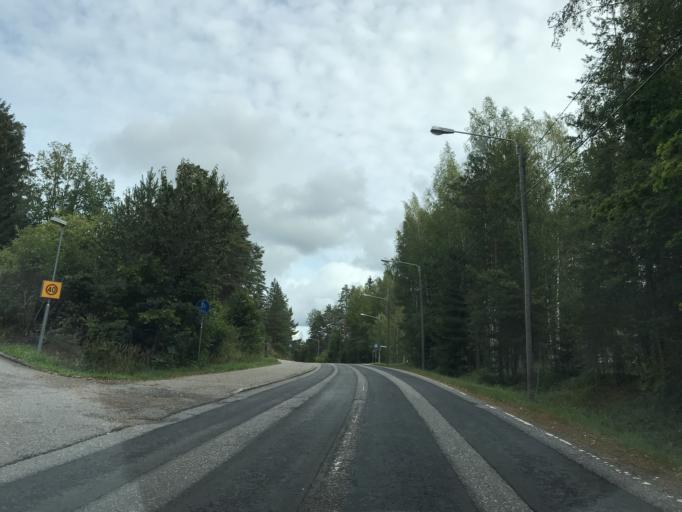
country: FI
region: Paijanne Tavastia
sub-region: Lahti
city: Nastola
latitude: 61.0137
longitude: 25.8138
